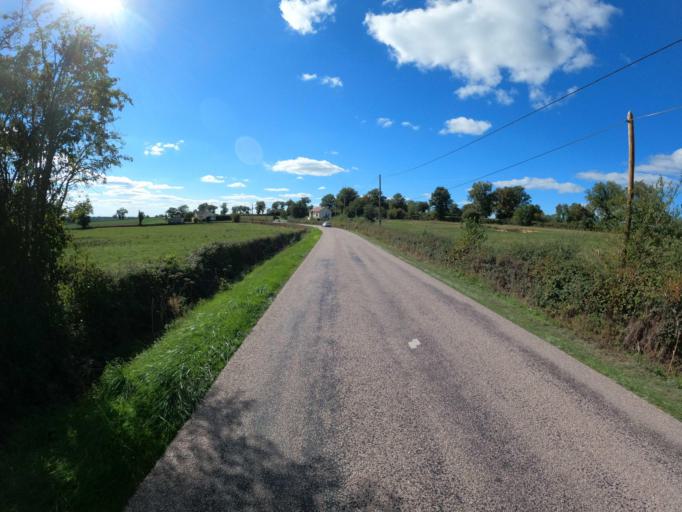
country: FR
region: Auvergne
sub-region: Departement de l'Allier
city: Buxieres-les-Mines
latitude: 46.4058
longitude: 3.0362
